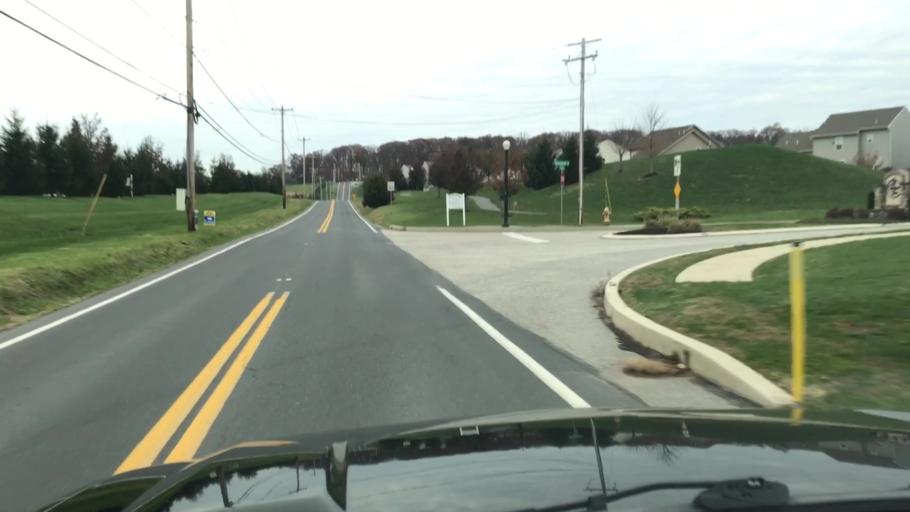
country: US
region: Pennsylvania
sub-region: Cumberland County
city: Shiremanstown
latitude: 40.1901
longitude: -76.9566
